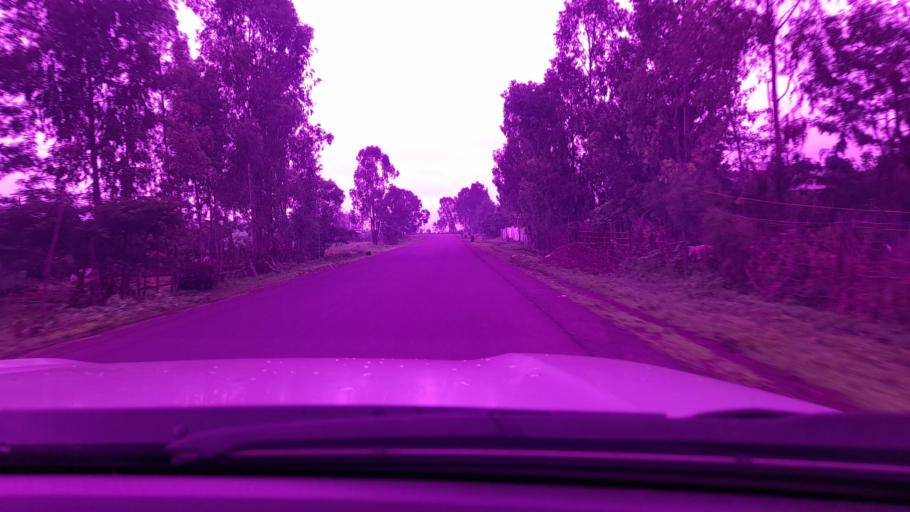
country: ET
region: Oromiya
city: Waliso
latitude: 8.2742
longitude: 37.6703
